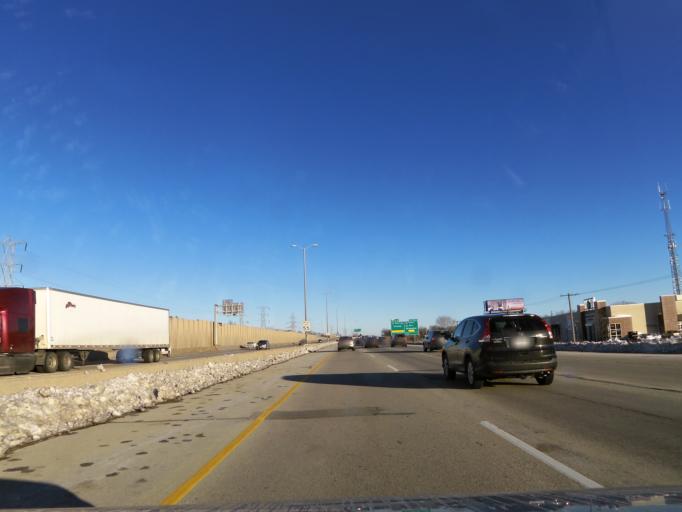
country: US
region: Wisconsin
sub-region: Milwaukee County
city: Greendale
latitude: 42.9624
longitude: -87.9845
